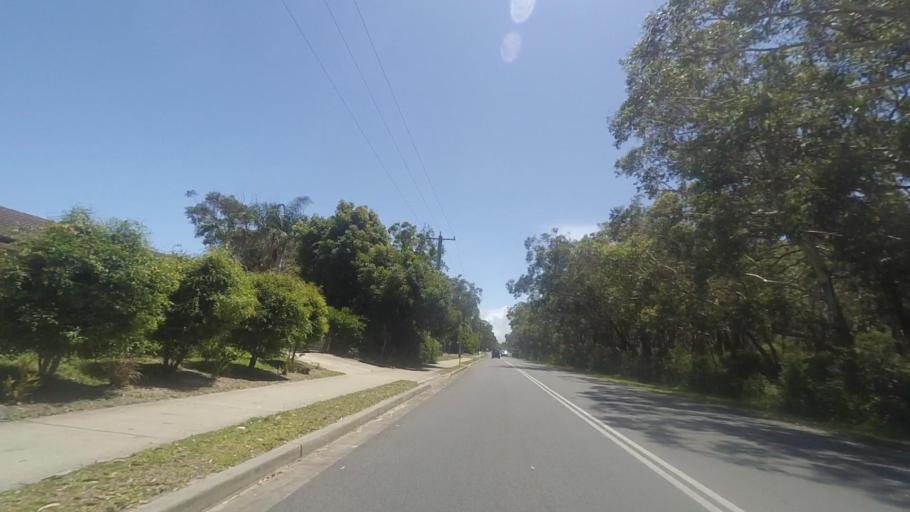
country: AU
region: New South Wales
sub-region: Great Lakes
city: Hawks Nest
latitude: -32.6704
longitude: 152.1778
